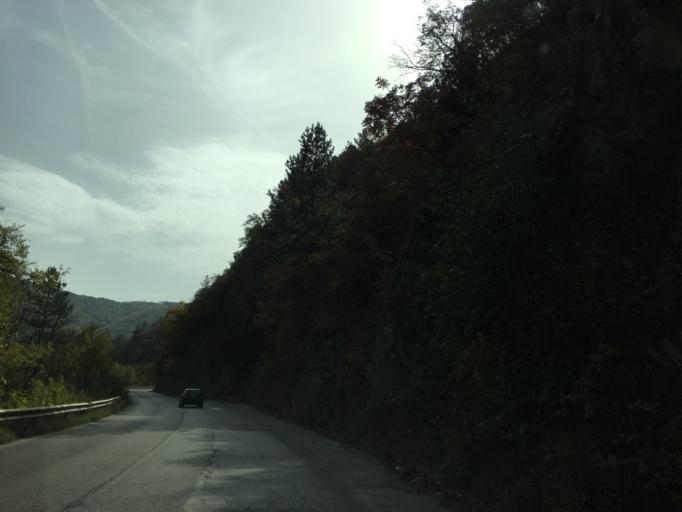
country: BG
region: Sofia-Capital
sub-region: Stolichna Obshtina
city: Sofia
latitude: 42.5750
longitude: 23.4282
